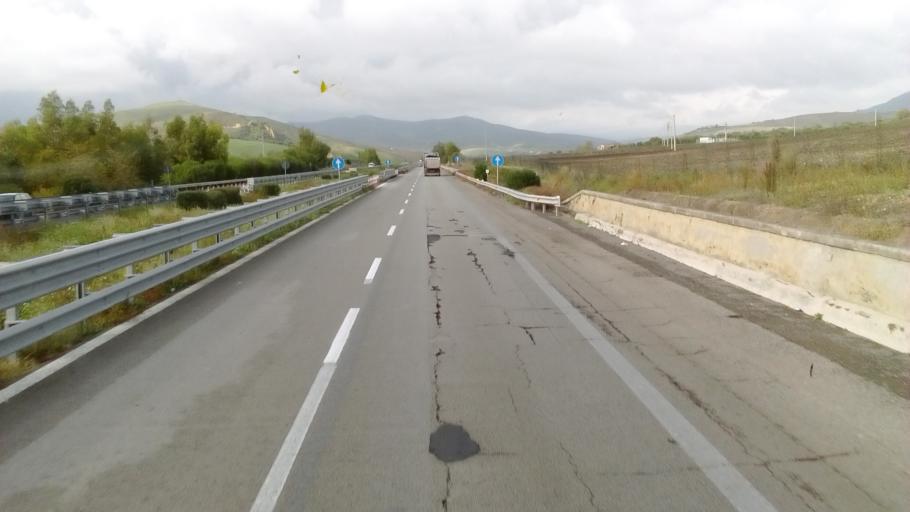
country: IT
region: Sicily
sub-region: Enna
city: Assoro
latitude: 37.5723
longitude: 14.4596
